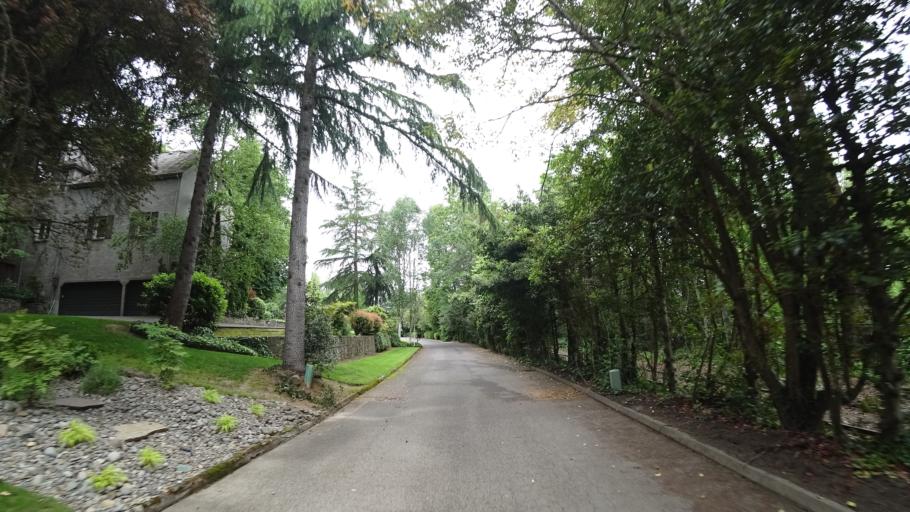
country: US
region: Oregon
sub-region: Clackamas County
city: Milwaukie
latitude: 45.4416
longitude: -122.6512
